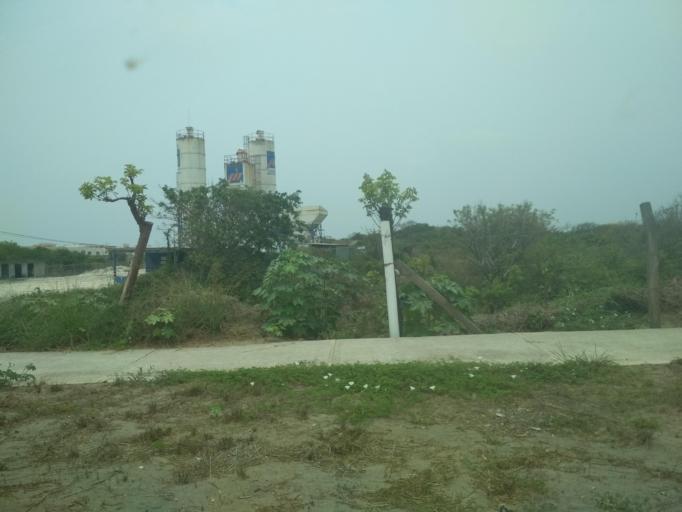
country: MX
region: Veracruz
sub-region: Alvarado
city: Playa de la Libertad
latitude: 19.0609
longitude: -96.0726
